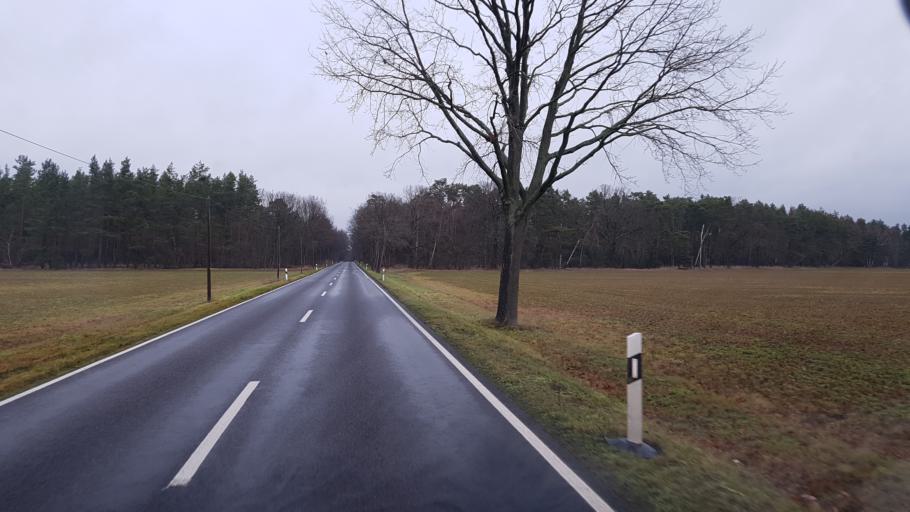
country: DE
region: Brandenburg
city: Altdobern
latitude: 51.6923
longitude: 14.0266
